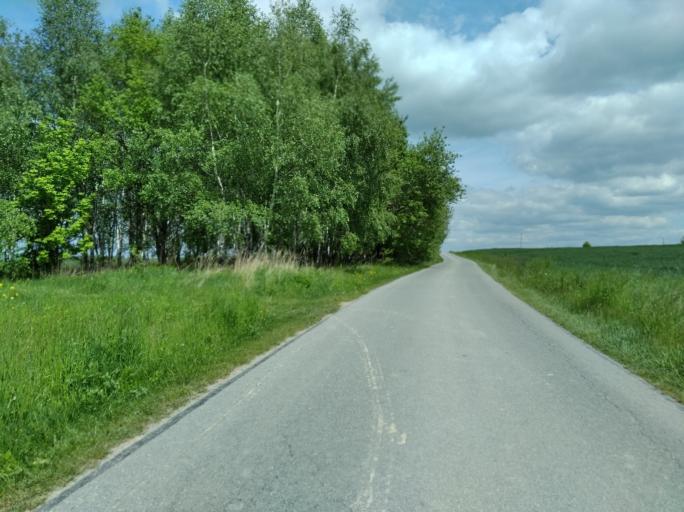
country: PL
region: Subcarpathian Voivodeship
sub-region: Powiat ropczycko-sedziszowski
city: Wielopole Skrzynskie
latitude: 49.9084
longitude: 21.5949
